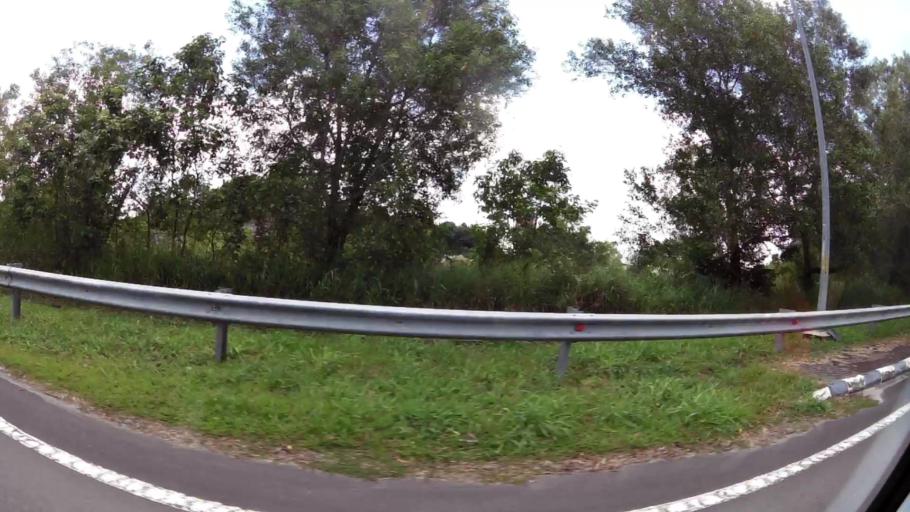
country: BN
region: Brunei and Muara
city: Bandar Seri Begawan
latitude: 4.9318
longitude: 114.9740
